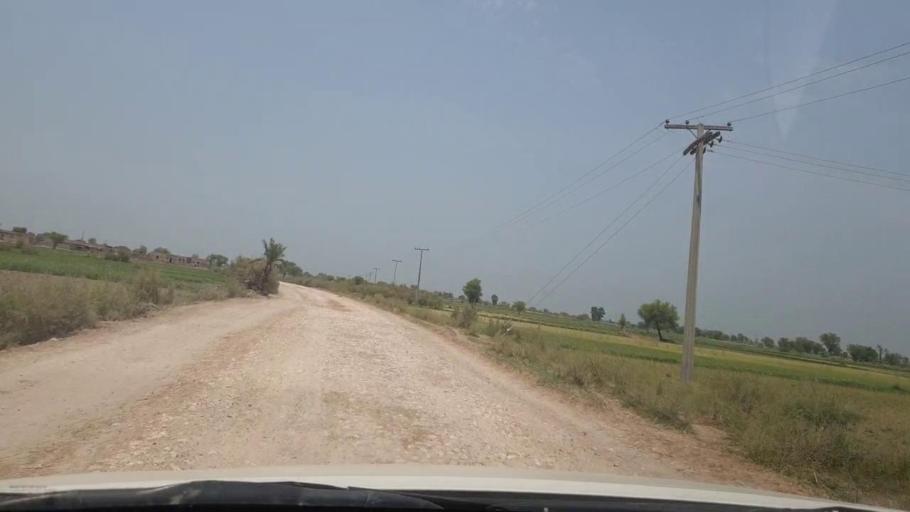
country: PK
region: Sindh
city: Rustam jo Goth
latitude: 28.0341
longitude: 68.7570
